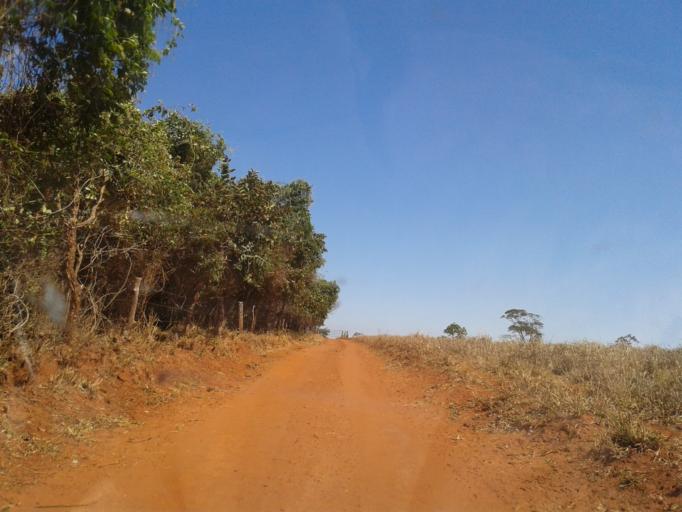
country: BR
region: Minas Gerais
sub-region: Monte Alegre De Minas
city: Monte Alegre de Minas
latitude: -18.8281
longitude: -49.1244
